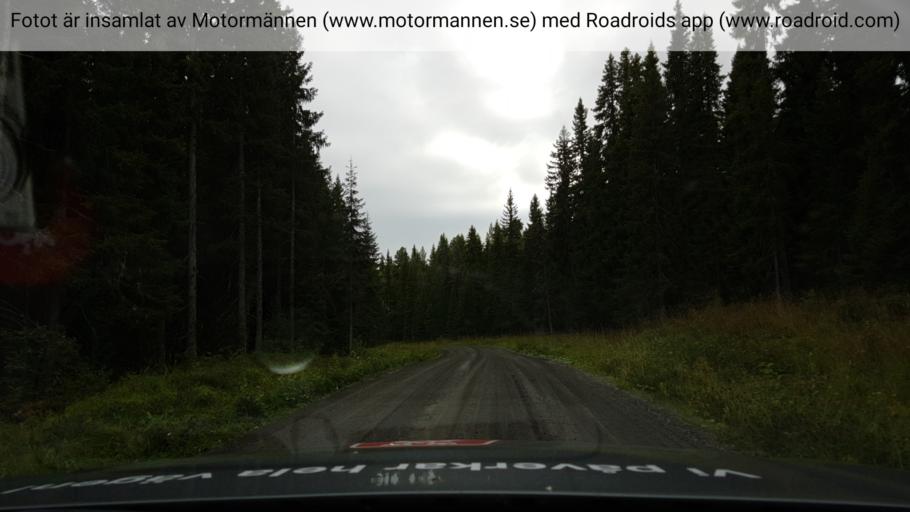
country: SE
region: Jaemtland
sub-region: Krokoms Kommun
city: Valla
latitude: 63.3922
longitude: 14.0627
